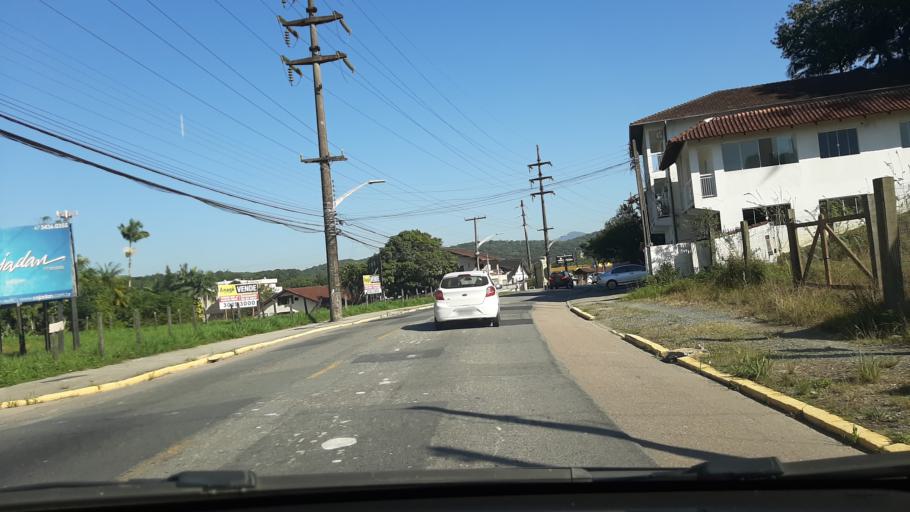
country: BR
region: Santa Catarina
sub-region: Joinville
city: Joinville
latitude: -26.3188
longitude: -48.8657
